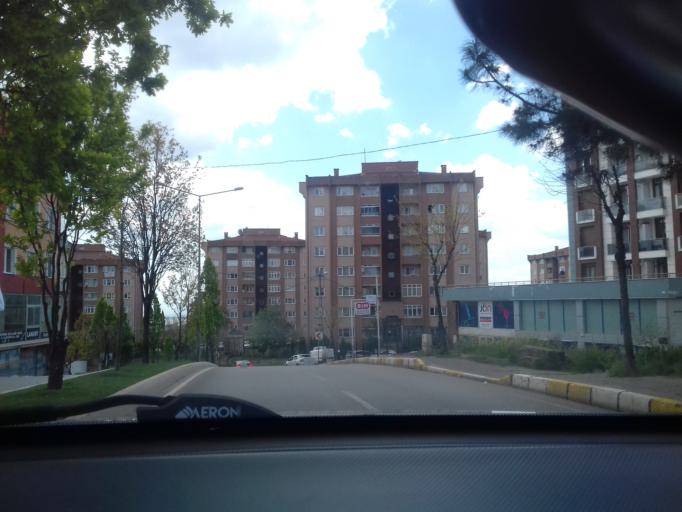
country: TR
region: Istanbul
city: Pendik
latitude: 40.9073
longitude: 29.2785
